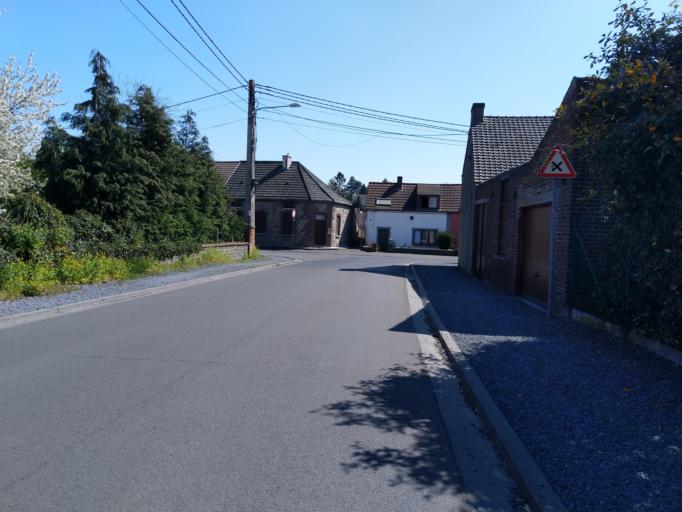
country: BE
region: Wallonia
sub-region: Province du Hainaut
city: Mons
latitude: 50.4773
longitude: 4.0087
